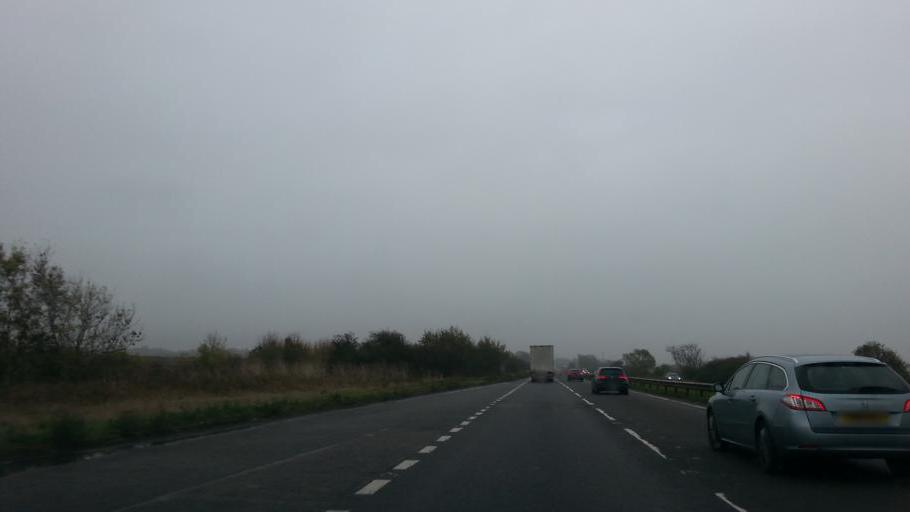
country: GB
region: England
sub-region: Lincolnshire
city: Long Bennington
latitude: 52.9794
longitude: -0.7449
